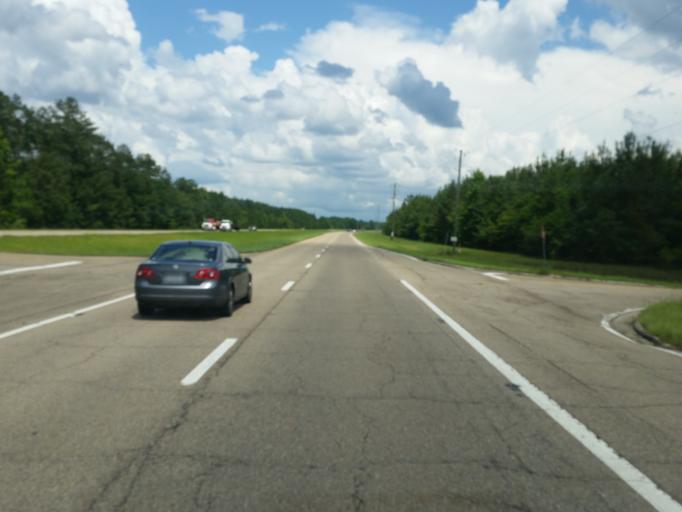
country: US
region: Mississippi
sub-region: Perry County
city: New Augusta
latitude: 31.1443
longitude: -88.8773
